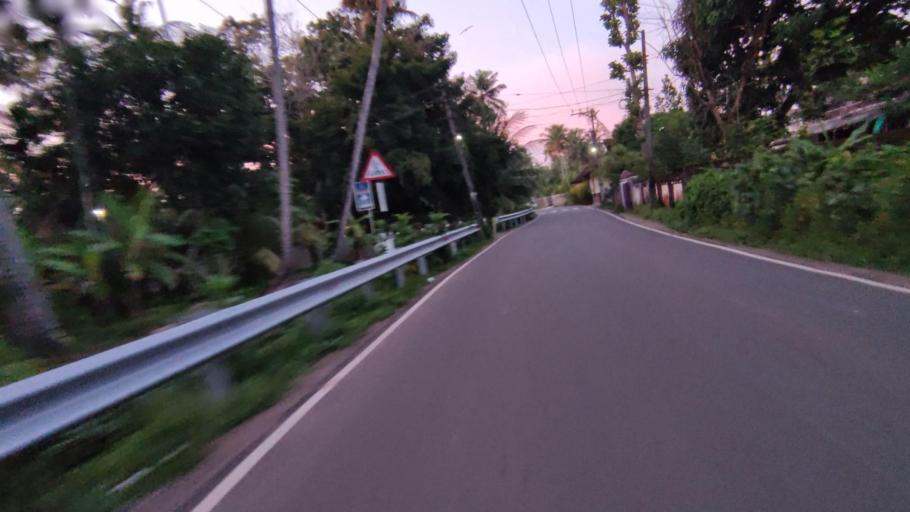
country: IN
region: Kerala
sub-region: Kottayam
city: Kottayam
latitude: 9.5848
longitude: 76.4361
